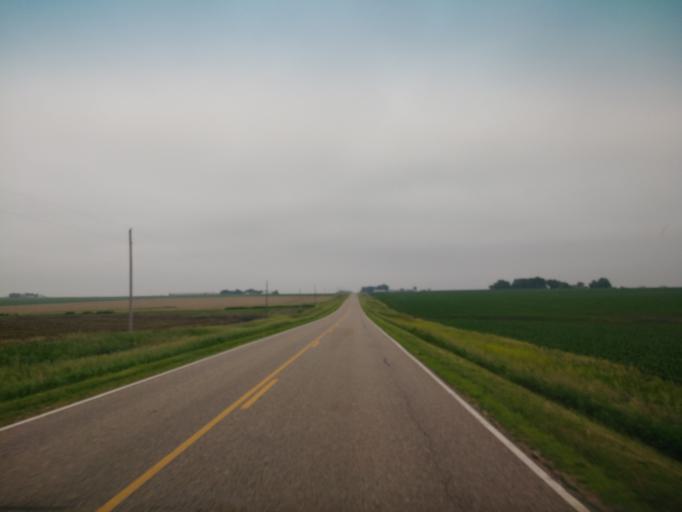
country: US
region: Iowa
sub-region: Sioux County
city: Alton
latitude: 43.0002
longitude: -95.8995
